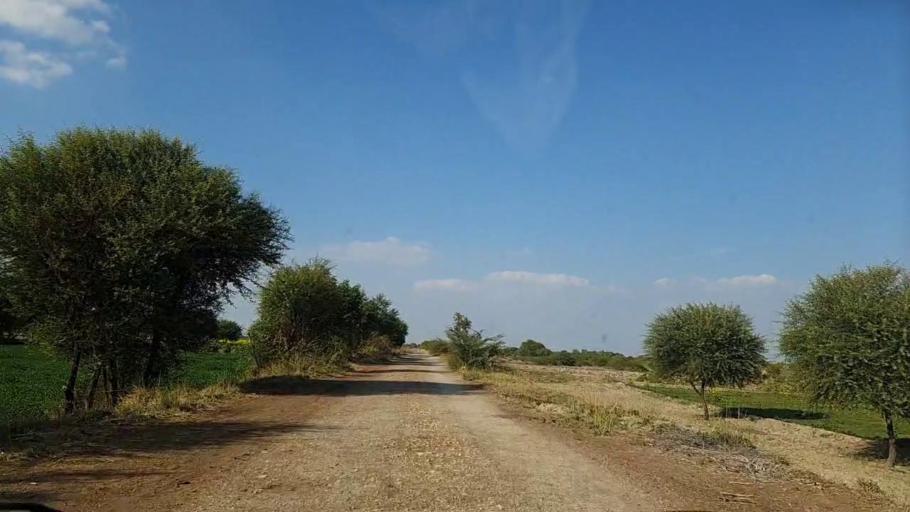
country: PK
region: Sindh
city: Pithoro
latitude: 25.6187
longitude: 69.3555
